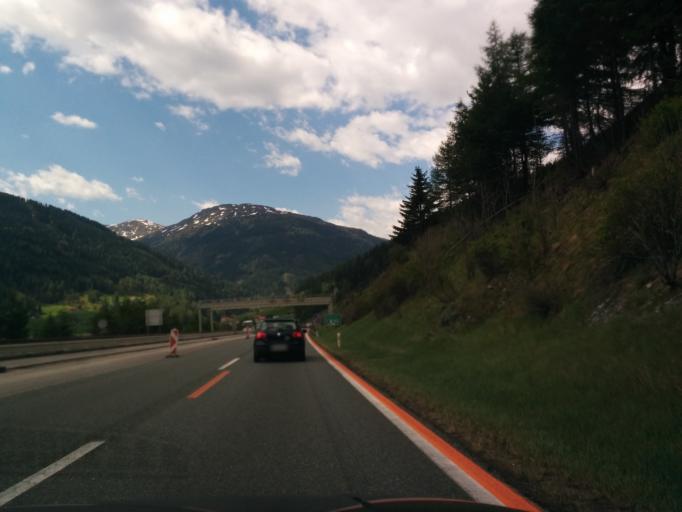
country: AT
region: Tyrol
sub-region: Politischer Bezirk Innsbruck Land
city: Gries am Brenner
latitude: 47.0447
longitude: 11.4796
